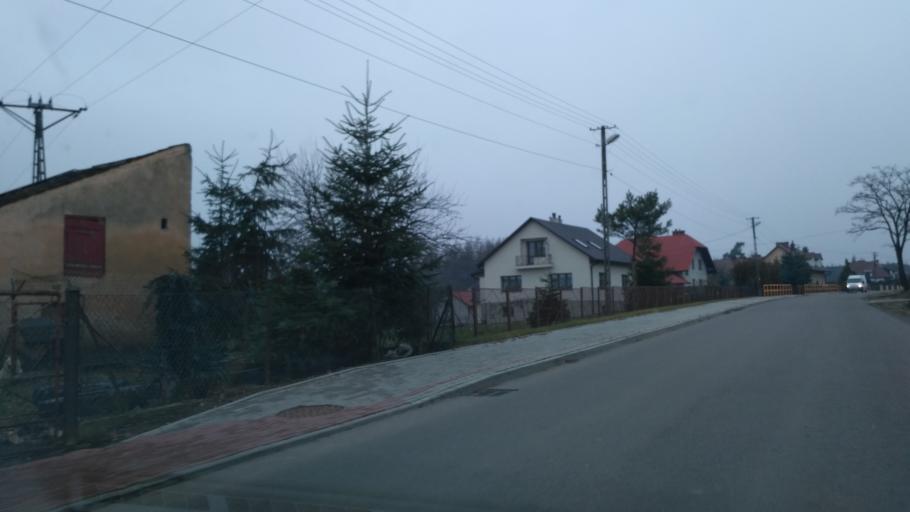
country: PL
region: Subcarpathian Voivodeship
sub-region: Powiat jaroslawski
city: Pawlosiow
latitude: 49.9794
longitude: 22.6388
